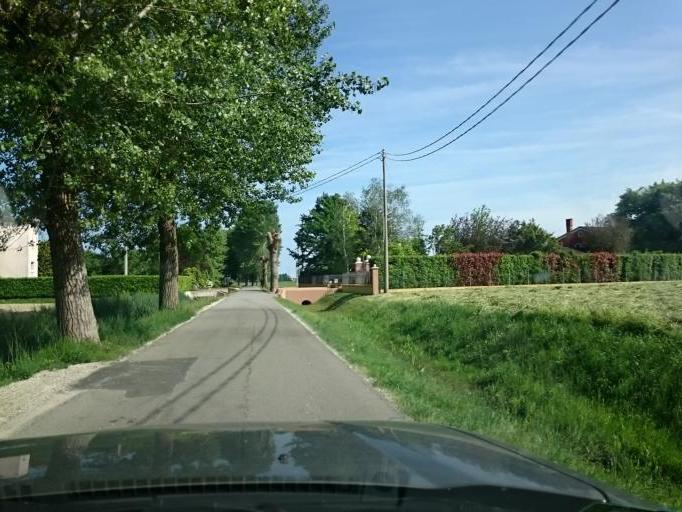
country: IT
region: Veneto
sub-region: Provincia di Venezia
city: Mira Taglio
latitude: 45.4277
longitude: 12.1575
